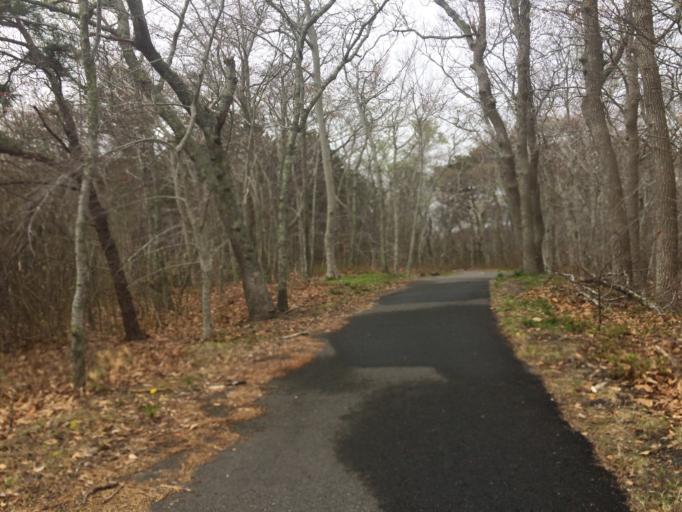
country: US
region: Massachusetts
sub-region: Barnstable County
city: Provincetown
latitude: 42.0651
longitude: -70.1959
